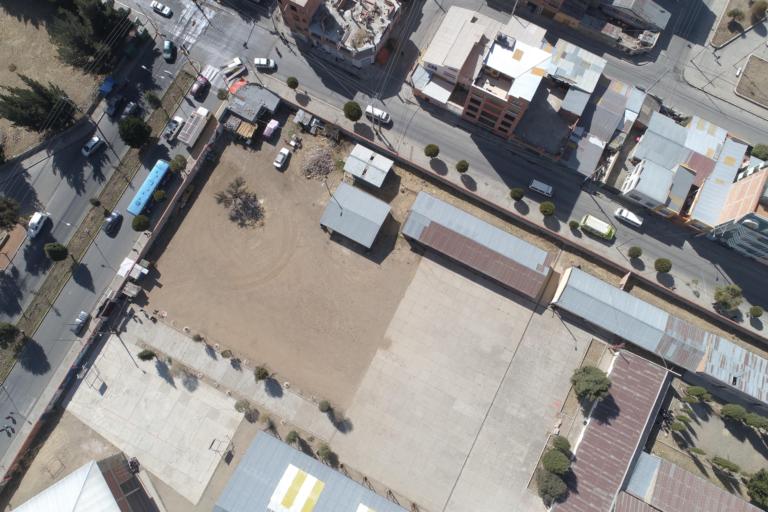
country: BO
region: La Paz
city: La Paz
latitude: -16.5271
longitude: -68.1516
